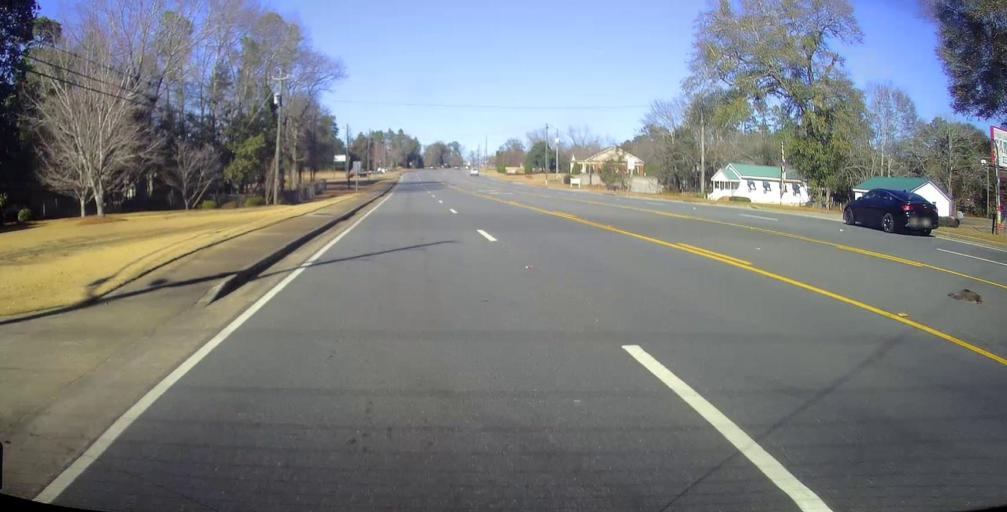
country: US
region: Georgia
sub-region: Taylor County
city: Butler
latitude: 32.5486
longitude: -84.2408
